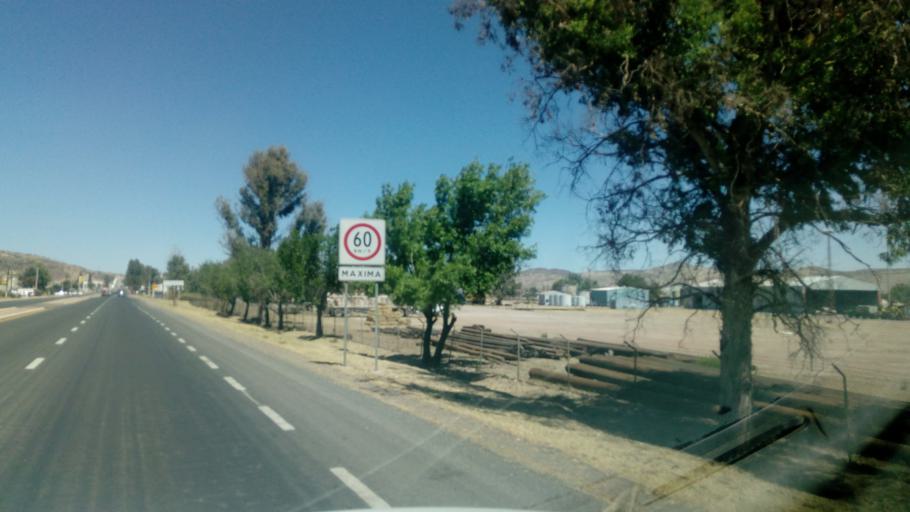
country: MX
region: Durango
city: Victoria de Durango
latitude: 24.0735
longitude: -104.6597
